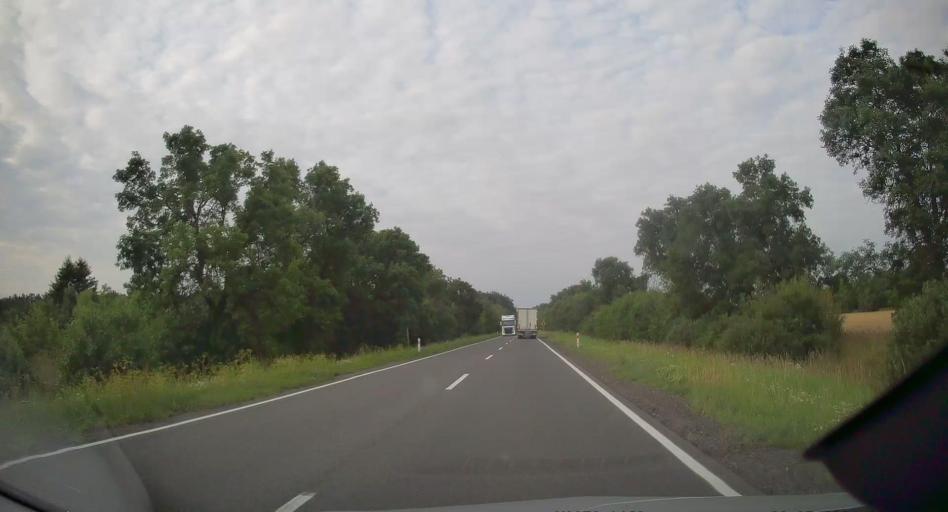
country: PL
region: Silesian Voivodeship
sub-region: Powiat czestochowski
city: Klomnice
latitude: 50.9457
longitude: 19.3938
